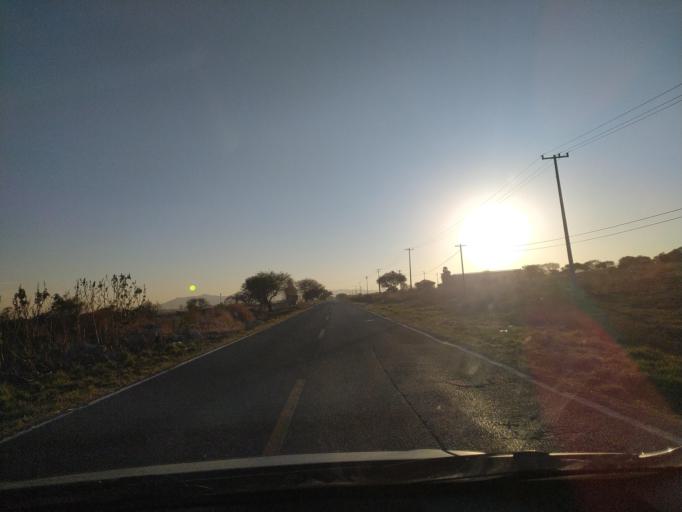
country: MX
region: Guanajuato
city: Ciudad Manuel Doblado
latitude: 20.7389
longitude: -101.9490
